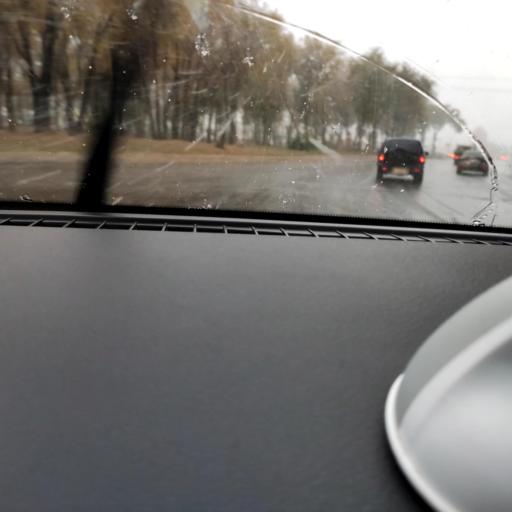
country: RU
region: Samara
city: Smyshlyayevka
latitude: 53.2251
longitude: 50.2902
